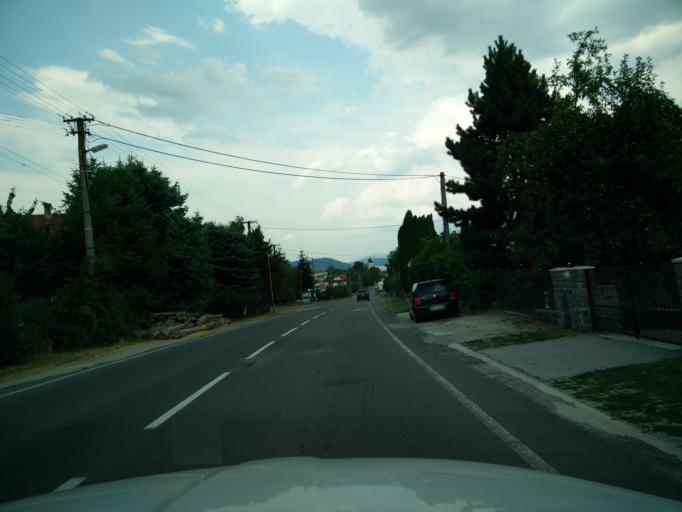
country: SK
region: Nitriansky
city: Novaky
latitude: 48.7902
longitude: 18.4775
